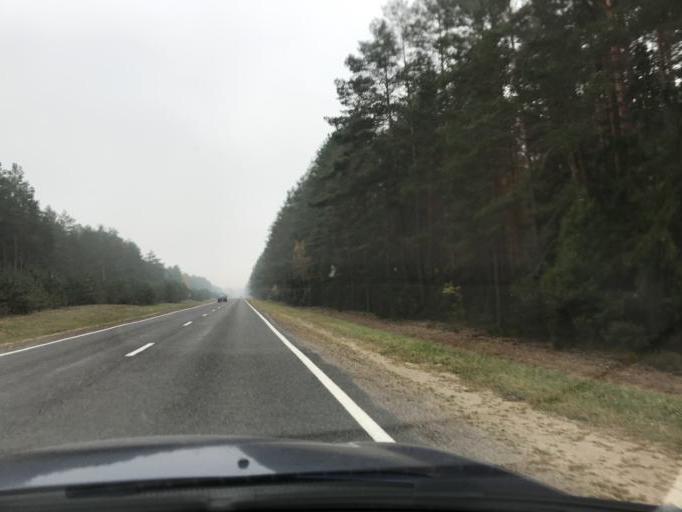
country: LT
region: Alytaus apskritis
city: Druskininkai
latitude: 53.8617
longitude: 23.8931
